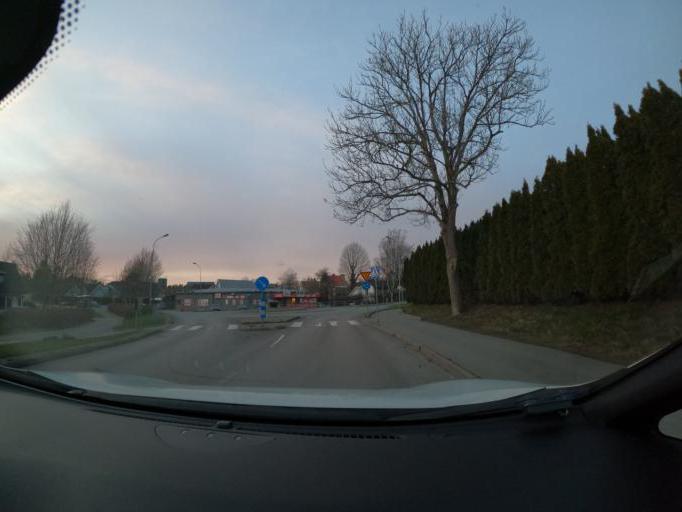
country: SE
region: Vaestra Goetaland
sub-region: Harryda Kommun
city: Molnlycke
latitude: 57.6475
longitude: 12.1237
